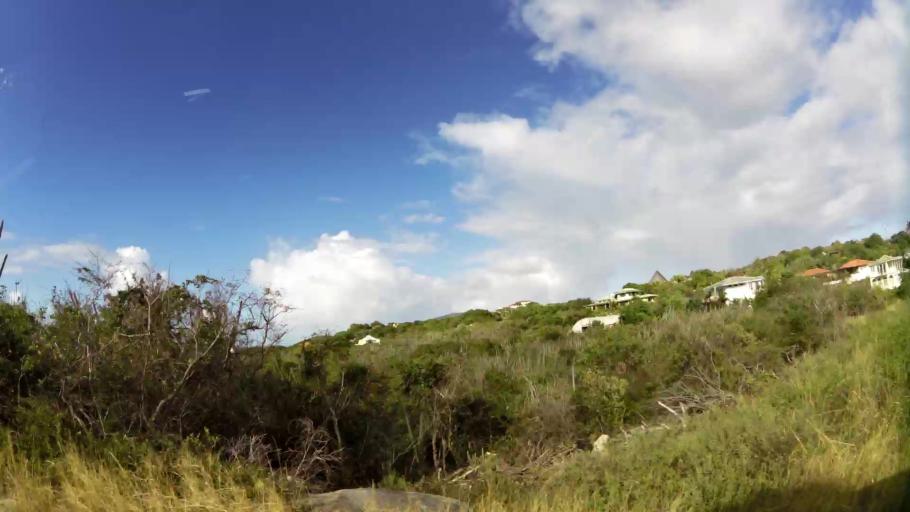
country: VG
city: Tortola
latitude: 18.4343
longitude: -64.4326
